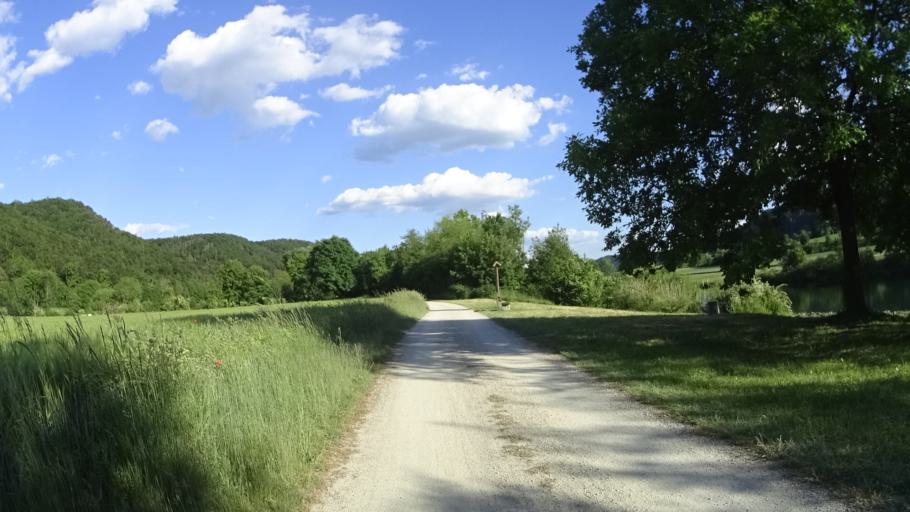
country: DE
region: Bavaria
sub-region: Upper Palatinate
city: Dietfurt
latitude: 49.0076
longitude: 11.6225
